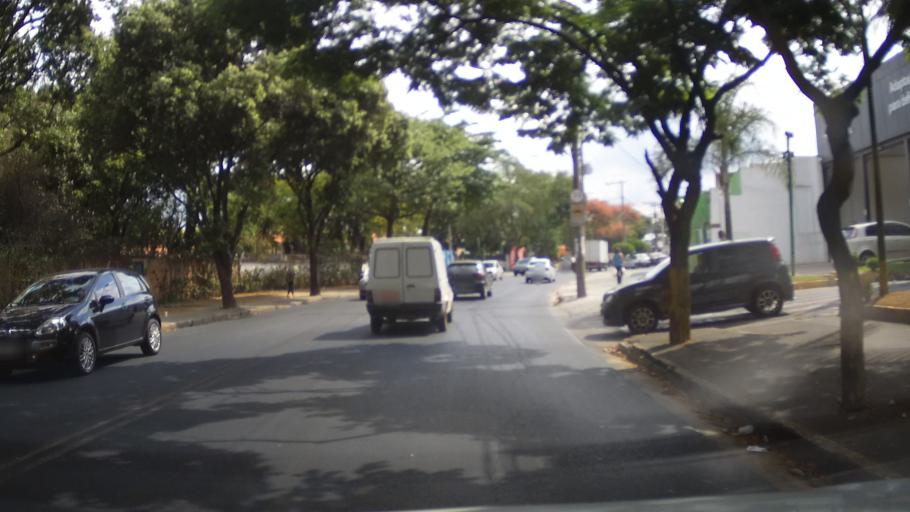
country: BR
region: Minas Gerais
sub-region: Belo Horizonte
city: Belo Horizonte
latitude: -19.8452
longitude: -43.9720
